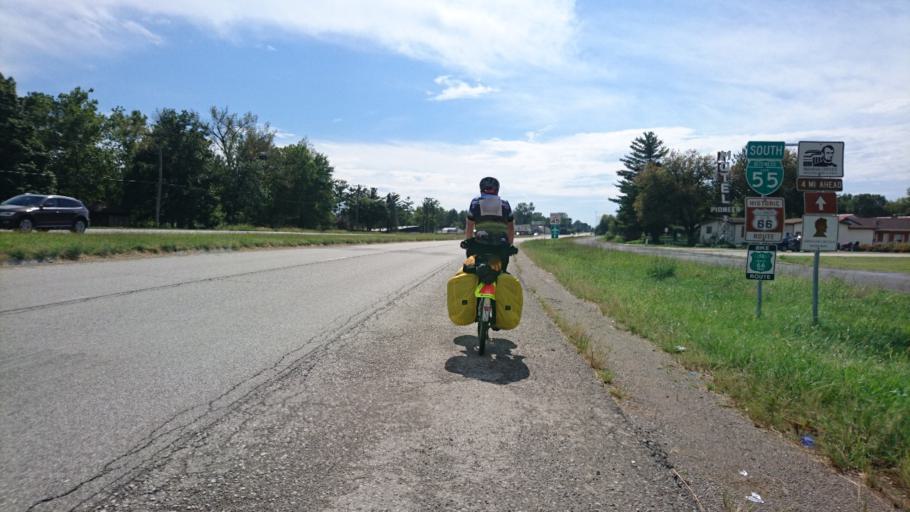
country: US
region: Illinois
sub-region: Sangamon County
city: Sherman
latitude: 39.8571
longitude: -89.6159
